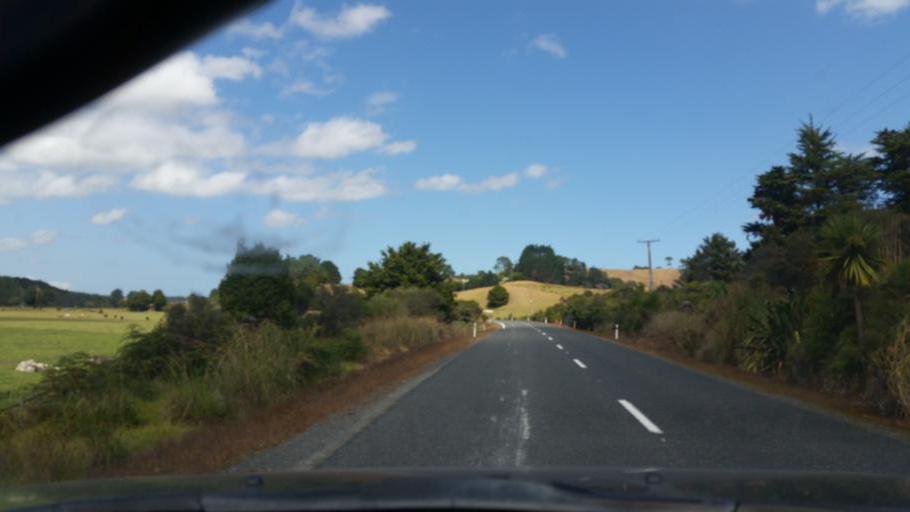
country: NZ
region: Northland
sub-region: Kaipara District
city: Dargaville
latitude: -35.8875
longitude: 173.8414
